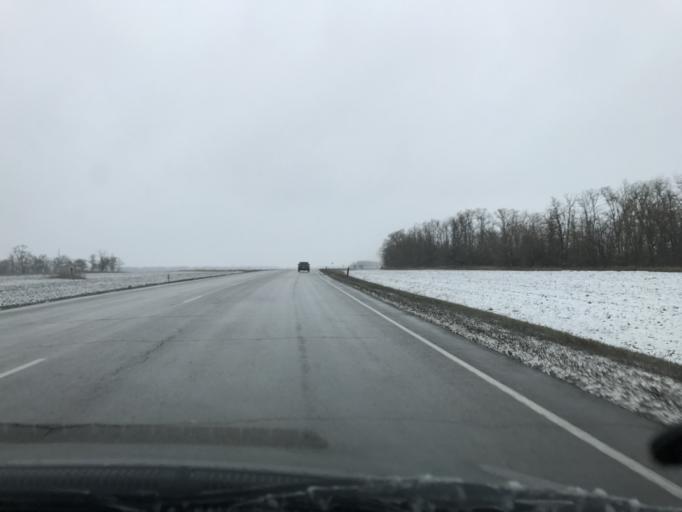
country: RU
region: Rostov
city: Yegorlykskaya
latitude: 46.6530
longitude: 40.5672
